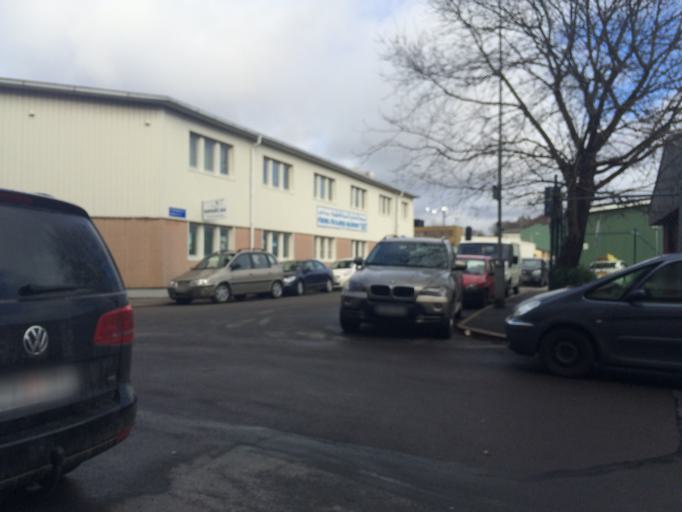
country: SE
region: Vaestra Goetaland
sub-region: Goteborg
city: Eriksbo
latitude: 57.7295
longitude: 12.0202
